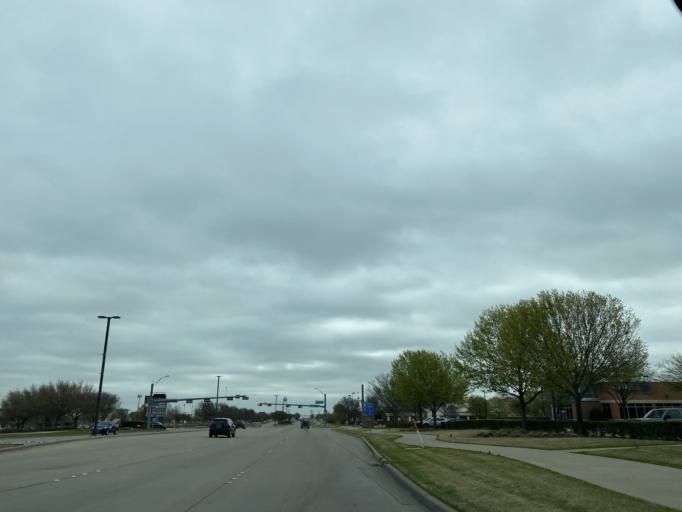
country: US
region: Texas
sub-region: Collin County
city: Allen
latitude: 33.1296
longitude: -96.6541
